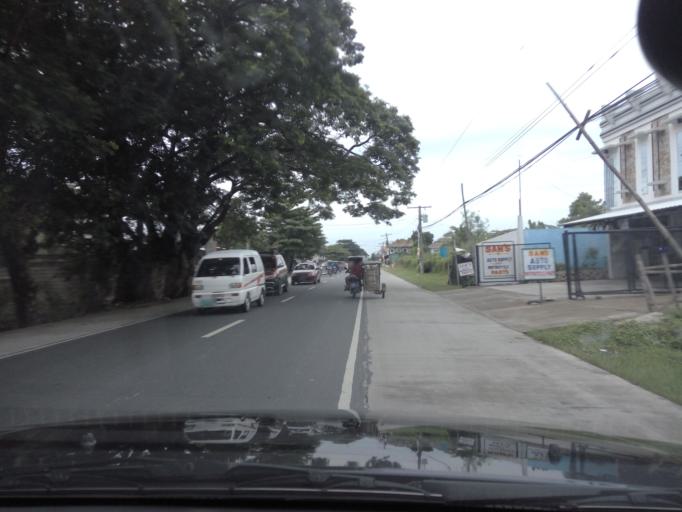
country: PH
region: Central Luzon
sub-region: Province of Nueva Ecija
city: Concepcion
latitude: 15.4483
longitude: 120.8072
